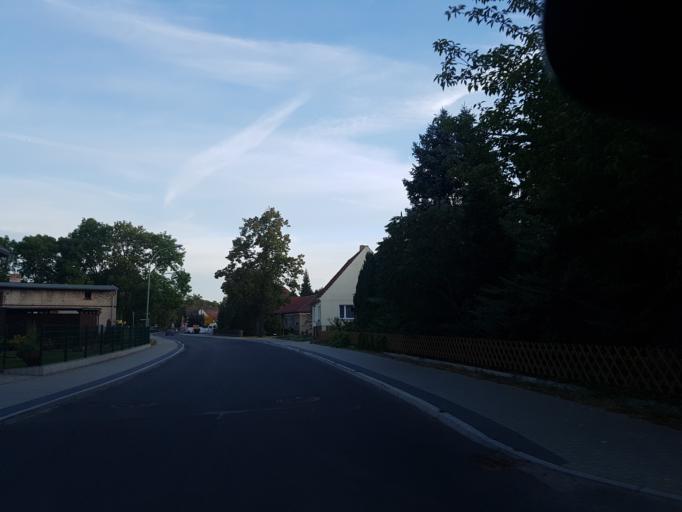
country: DE
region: Brandenburg
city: Sonnewalde
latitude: 51.6915
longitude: 13.6470
